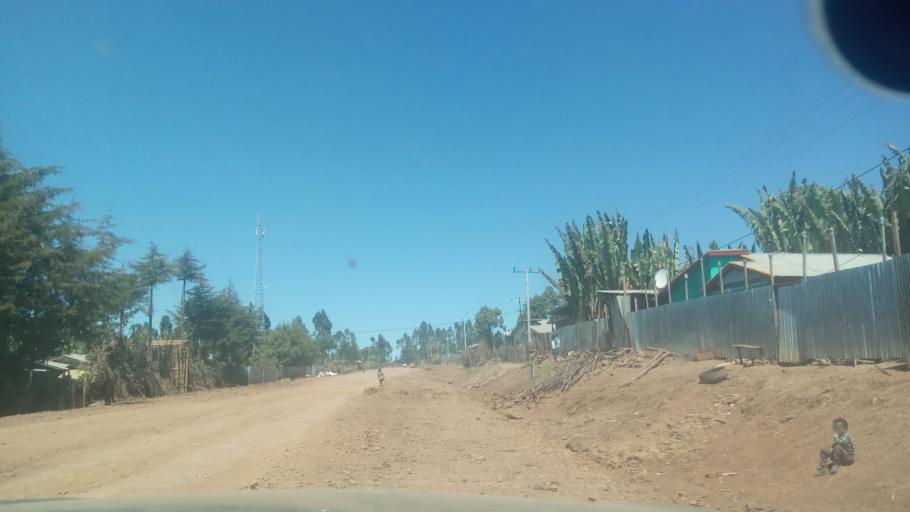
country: ET
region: Oromiya
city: Hagere Hiywet
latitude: 9.3285
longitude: 38.0755
